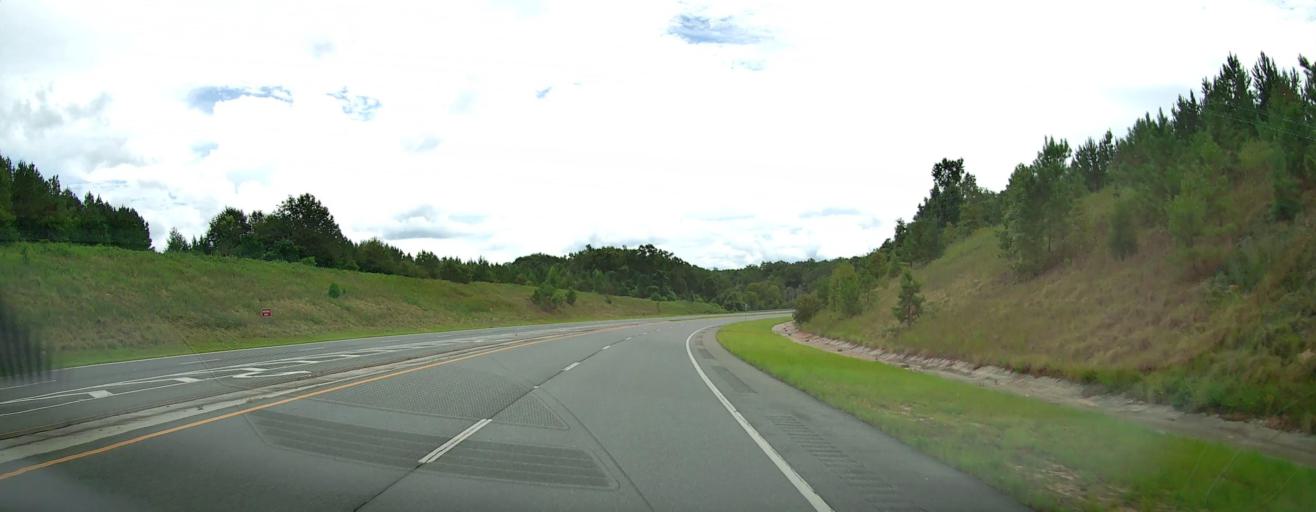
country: US
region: Georgia
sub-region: Schley County
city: Ellaville
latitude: 32.2518
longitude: -84.2980
